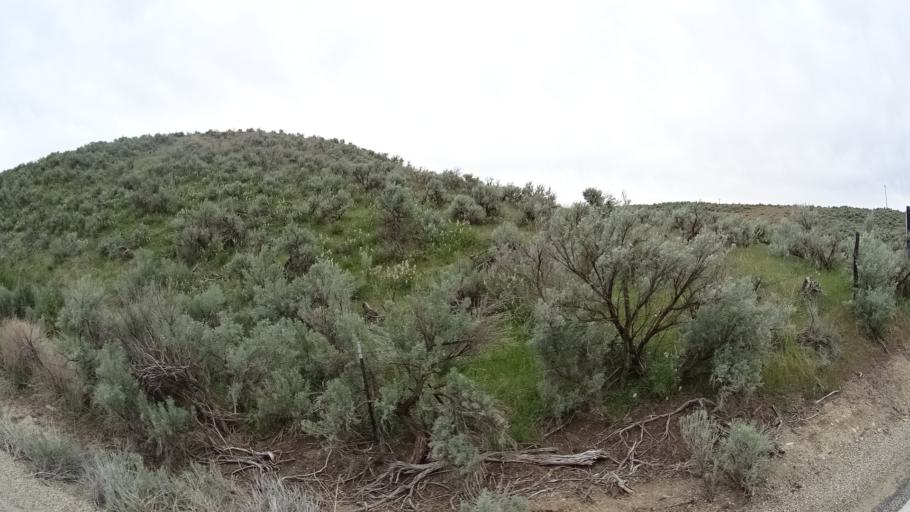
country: US
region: Idaho
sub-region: Ada County
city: Boise
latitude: 43.4781
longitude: -115.9911
